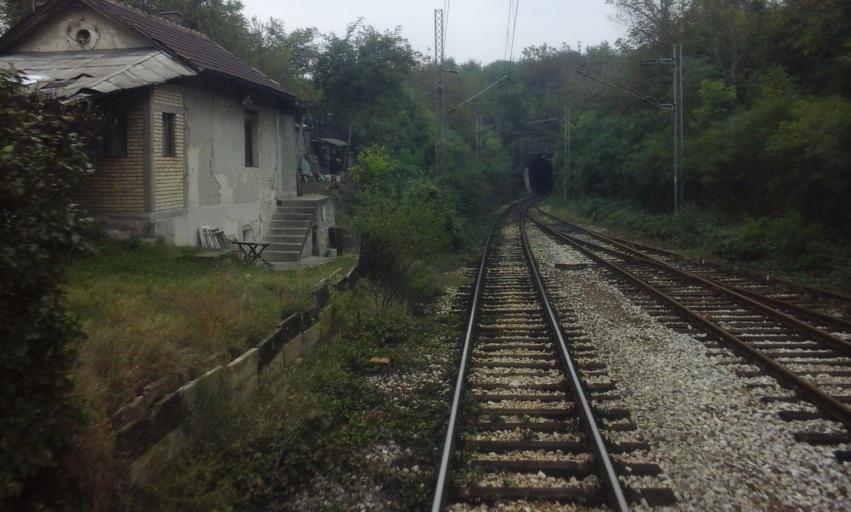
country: RS
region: Central Serbia
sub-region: Belgrade
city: Sopot
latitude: 44.5673
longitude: 20.5645
